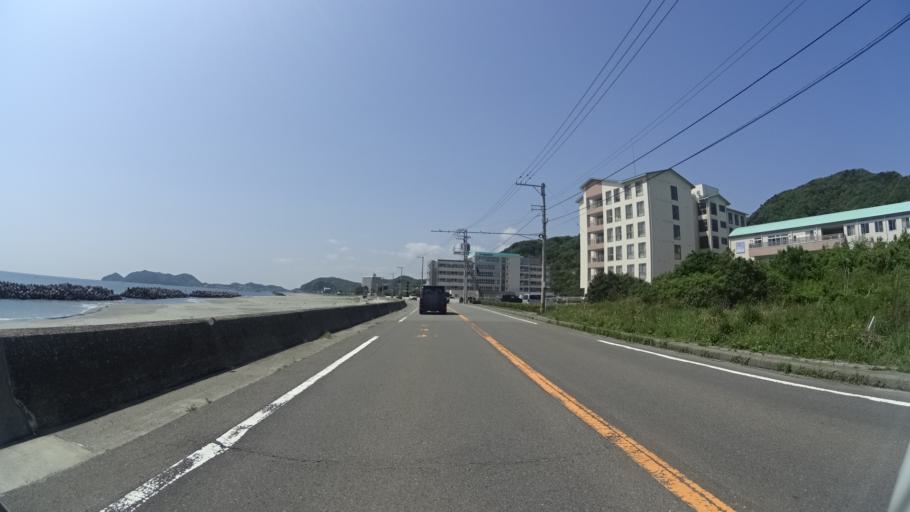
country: JP
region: Tokushima
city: Narutocho-mitsuishi
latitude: 34.2071
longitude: 134.6268
